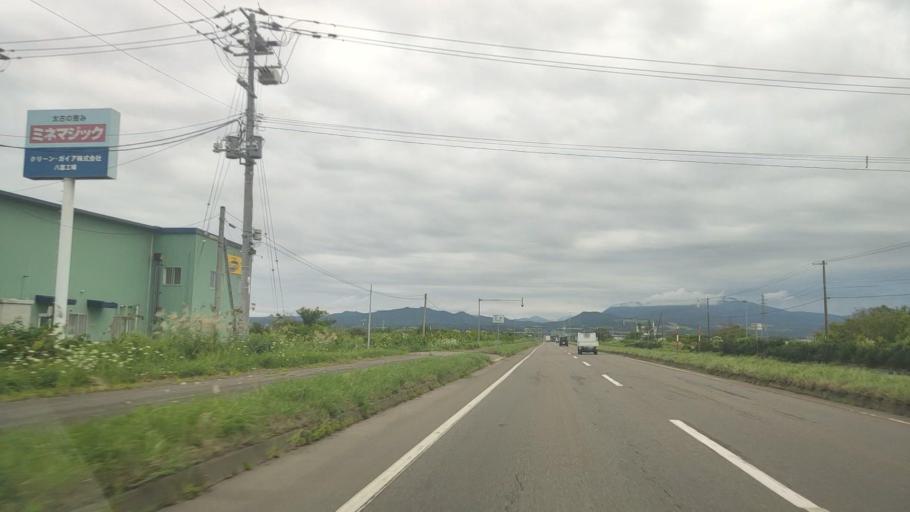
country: JP
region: Hokkaido
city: Nanae
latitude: 42.2740
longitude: 140.2724
